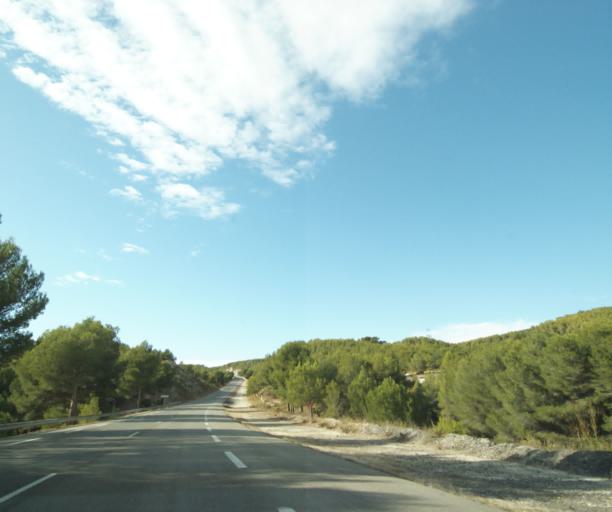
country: FR
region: Provence-Alpes-Cote d'Azur
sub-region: Departement des Bouches-du-Rhone
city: Sausset-les-Pins
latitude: 43.3422
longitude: 5.0968
